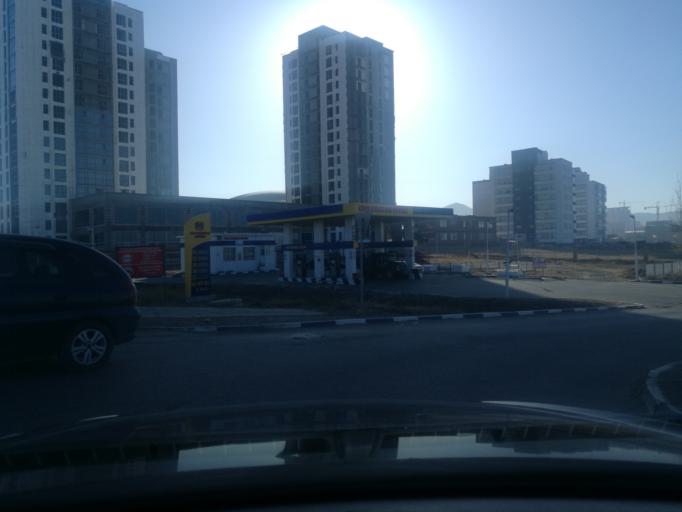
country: MN
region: Ulaanbaatar
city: Ulaanbaatar
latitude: 47.8563
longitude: 106.7799
